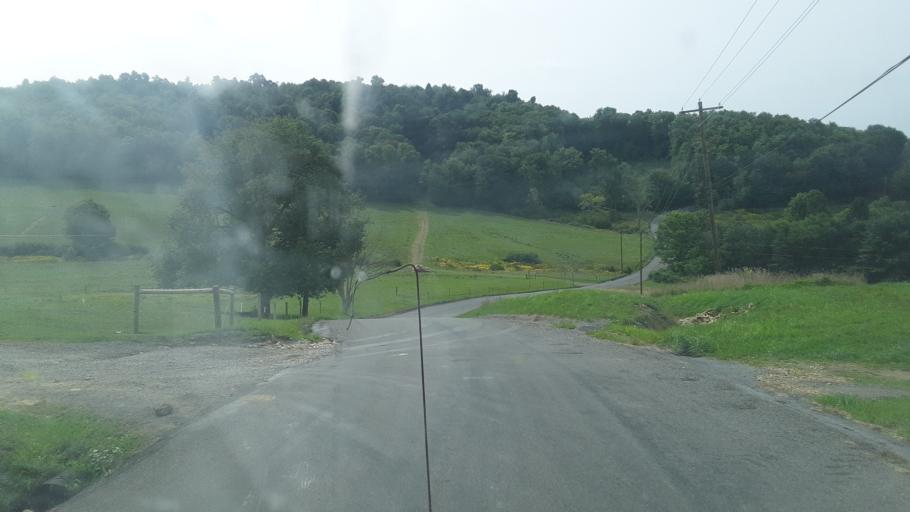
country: US
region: Pennsylvania
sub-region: Jefferson County
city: Punxsutawney
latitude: 40.9546
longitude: -79.1245
